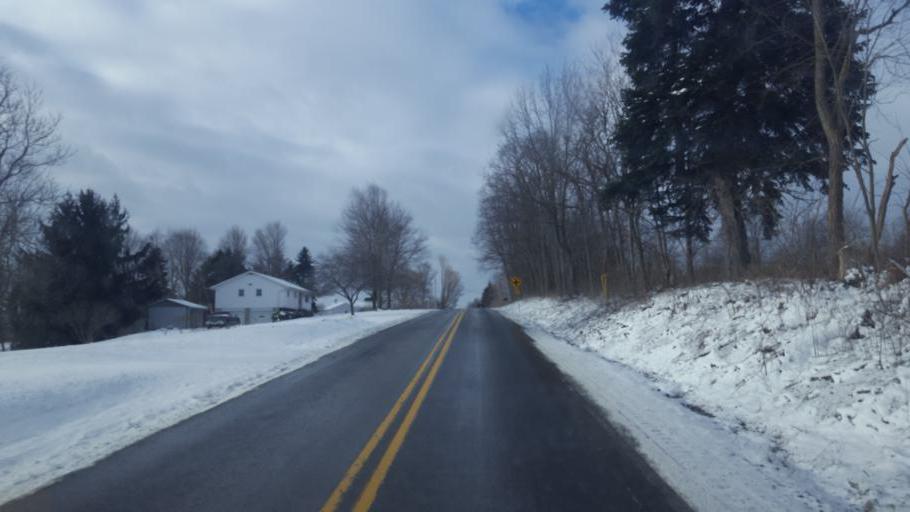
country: US
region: Pennsylvania
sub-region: Mercer County
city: Mercer
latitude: 41.1694
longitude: -80.2494
